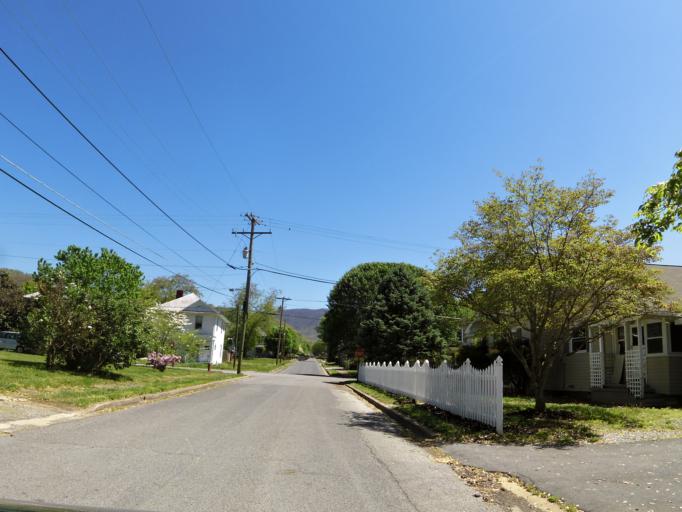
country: US
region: Tennessee
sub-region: Unicoi County
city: Erwin
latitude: 36.1428
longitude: -82.4203
